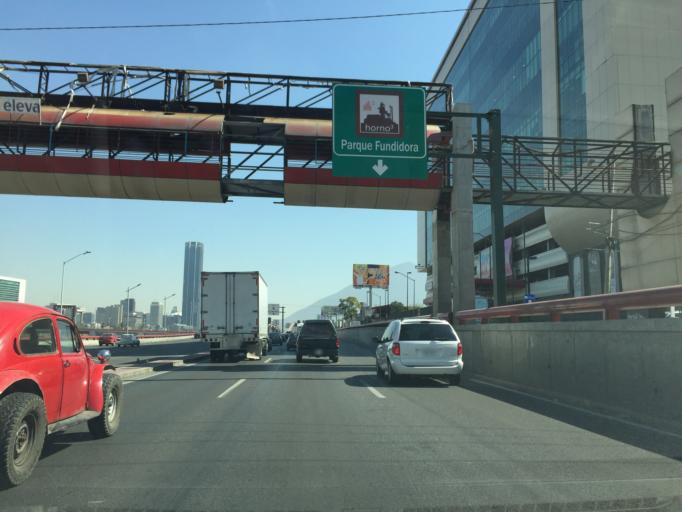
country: MX
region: Nuevo Leon
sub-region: Monterrey
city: Monterrey
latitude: 25.6653
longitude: -100.3312
